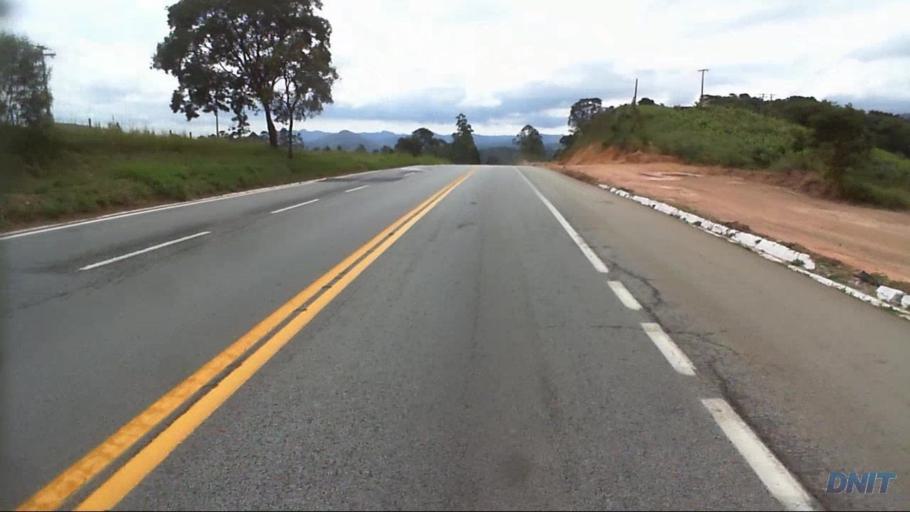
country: BR
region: Minas Gerais
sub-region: Caete
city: Caete
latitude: -19.7343
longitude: -43.5591
